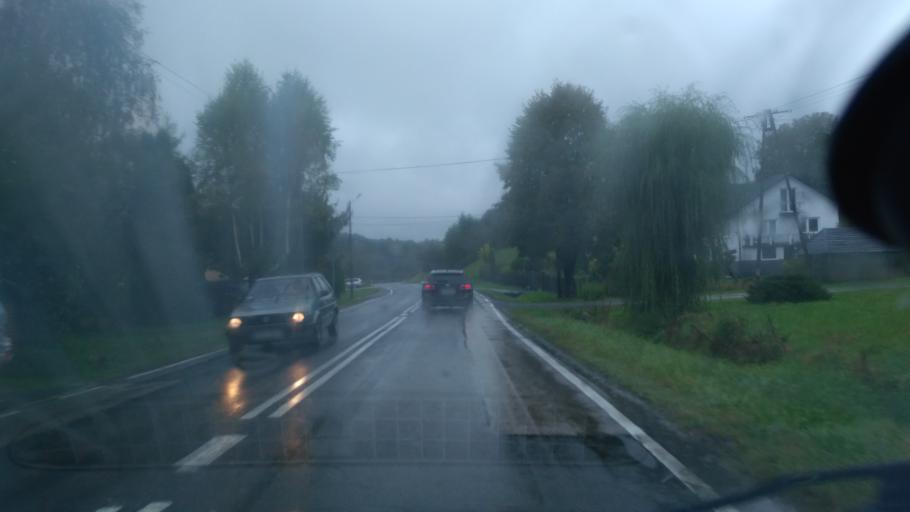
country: PL
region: Subcarpathian Voivodeship
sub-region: Powiat ropczycko-sedziszowski
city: Niedzwiada
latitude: 50.0046
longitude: 21.5572
